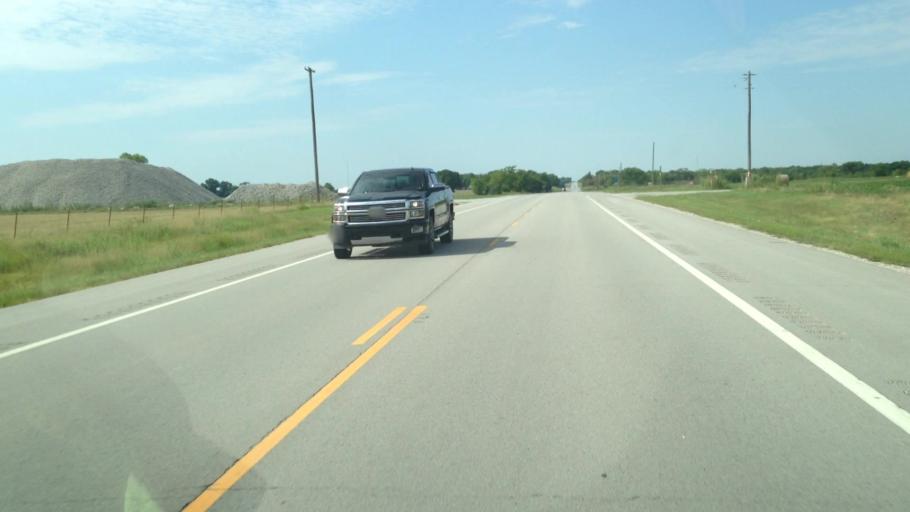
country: US
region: Kansas
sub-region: Labette County
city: Parsons
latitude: 37.2806
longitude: -95.2675
